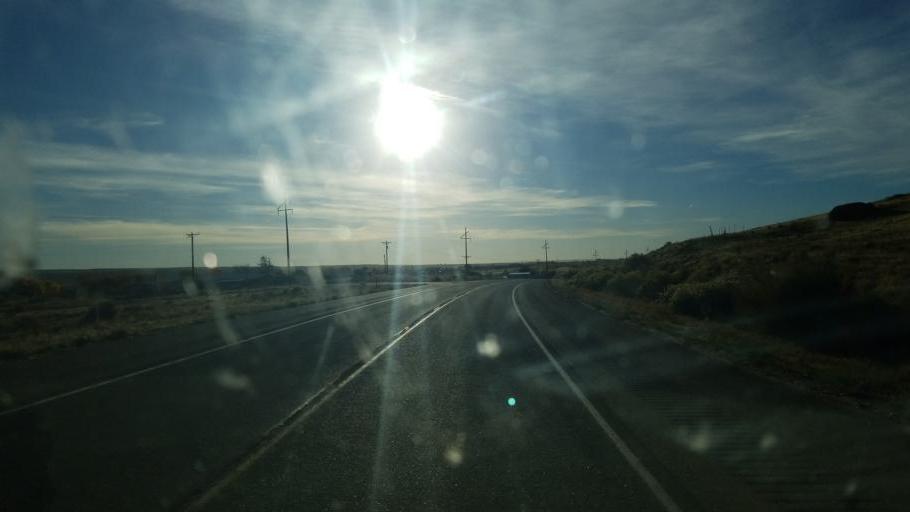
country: US
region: New Mexico
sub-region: San Juan County
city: Bloomfield
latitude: 36.7113
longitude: -107.8489
